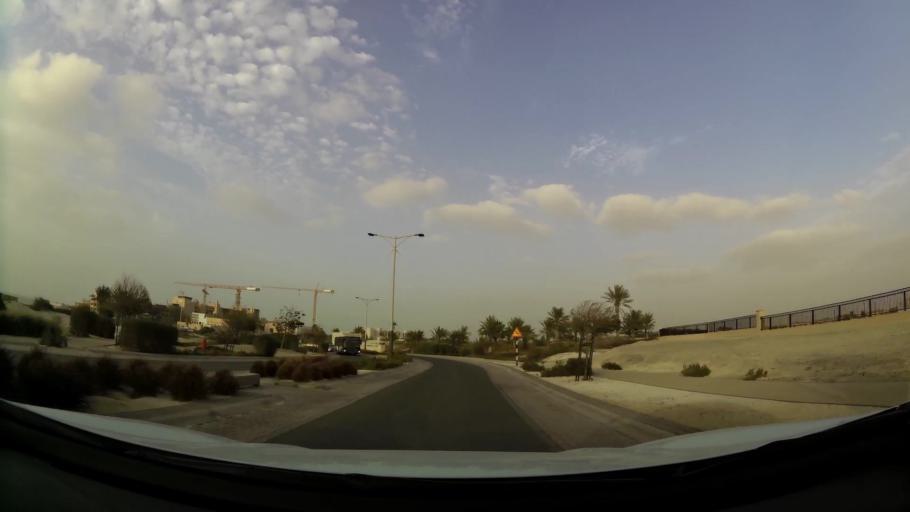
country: AE
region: Abu Dhabi
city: Abu Dhabi
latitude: 24.5381
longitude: 54.4292
